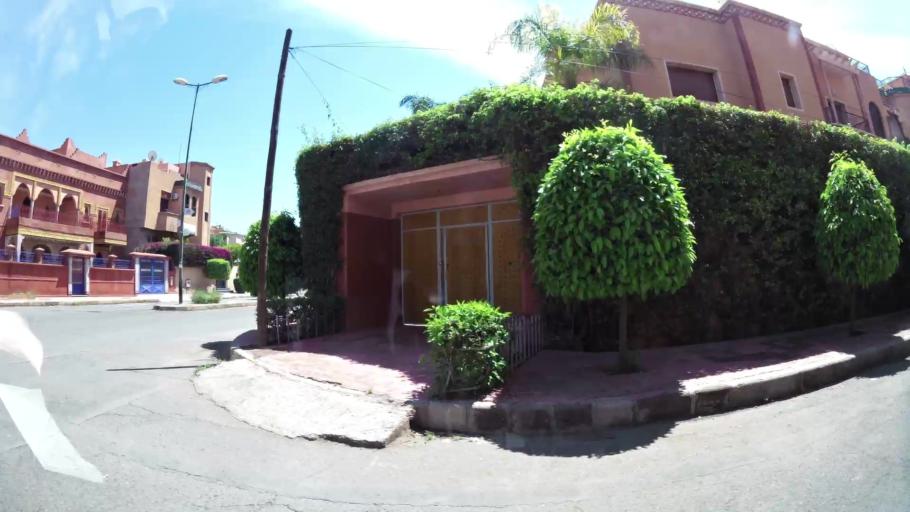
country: MA
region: Marrakech-Tensift-Al Haouz
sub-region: Marrakech
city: Marrakesh
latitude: 31.6402
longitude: -8.0621
